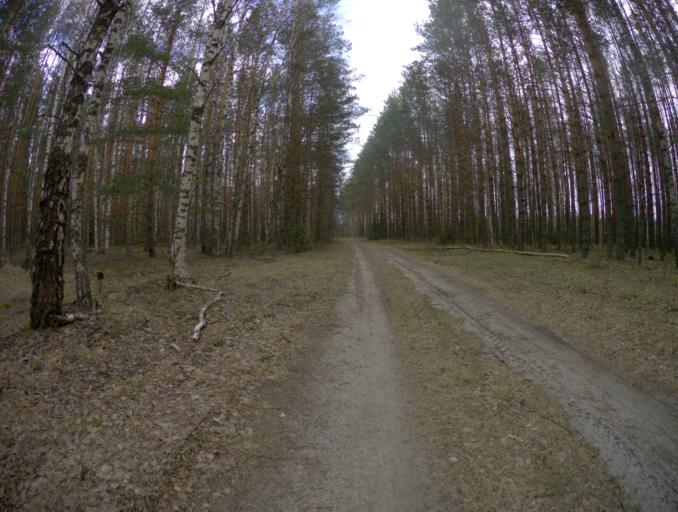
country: RU
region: Vladimir
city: Orgtrud
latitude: 56.0728
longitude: 40.7206
